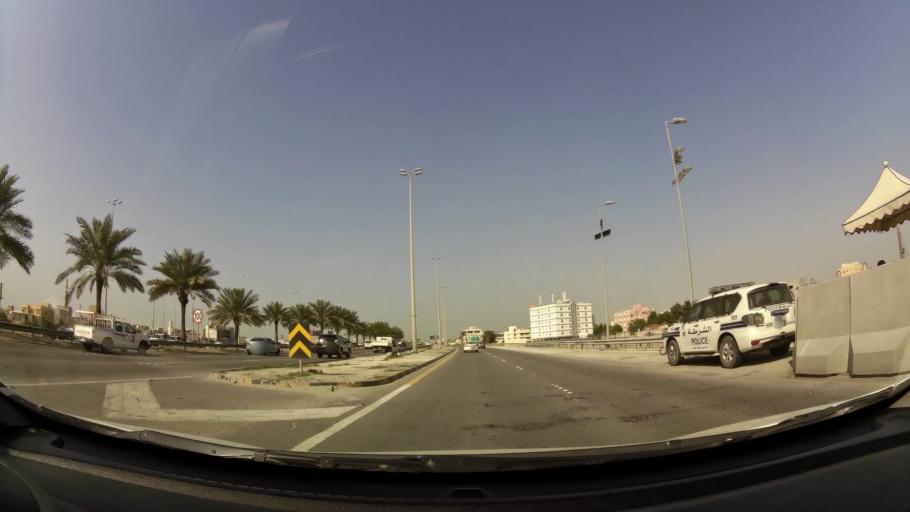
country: BH
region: Manama
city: Jidd Hafs
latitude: 26.2132
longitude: 50.5198
